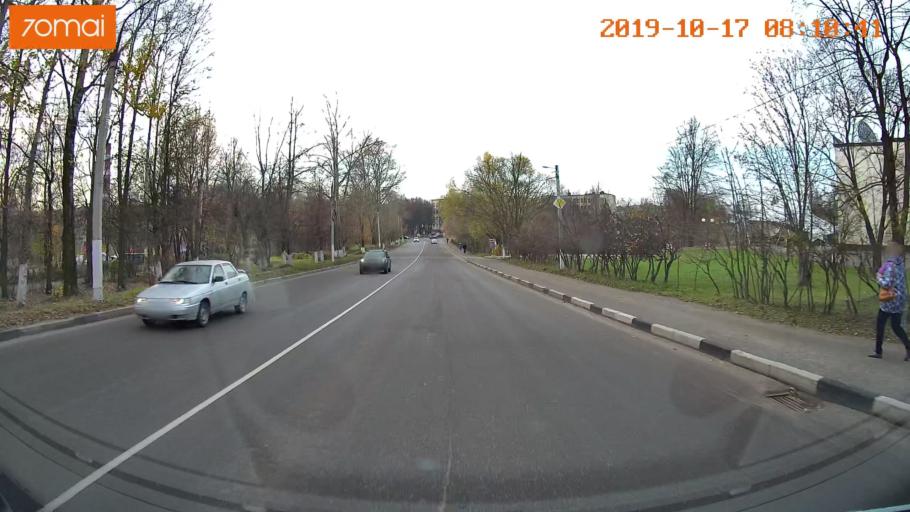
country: RU
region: Vladimir
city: Kol'chugino
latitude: 56.3065
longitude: 39.3770
